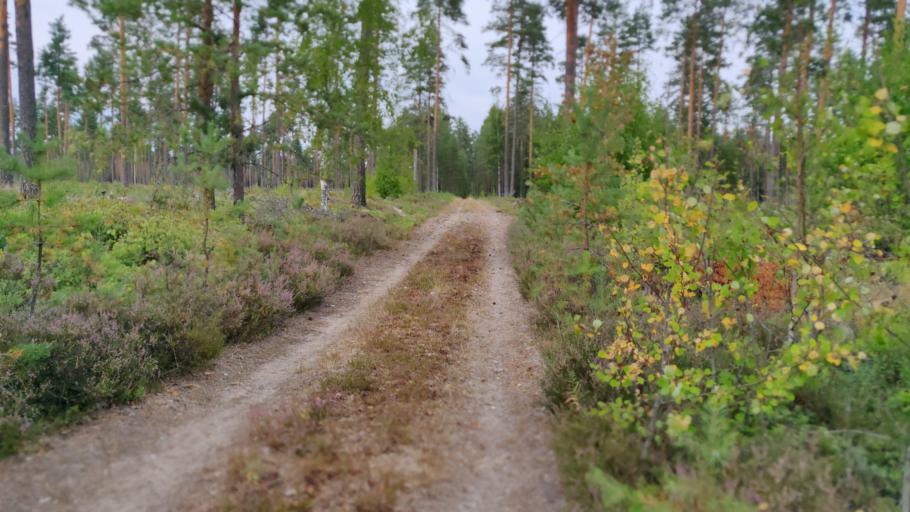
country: SE
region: Vaermland
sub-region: Hagfors Kommun
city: Hagfors
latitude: 60.0292
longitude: 13.5483
